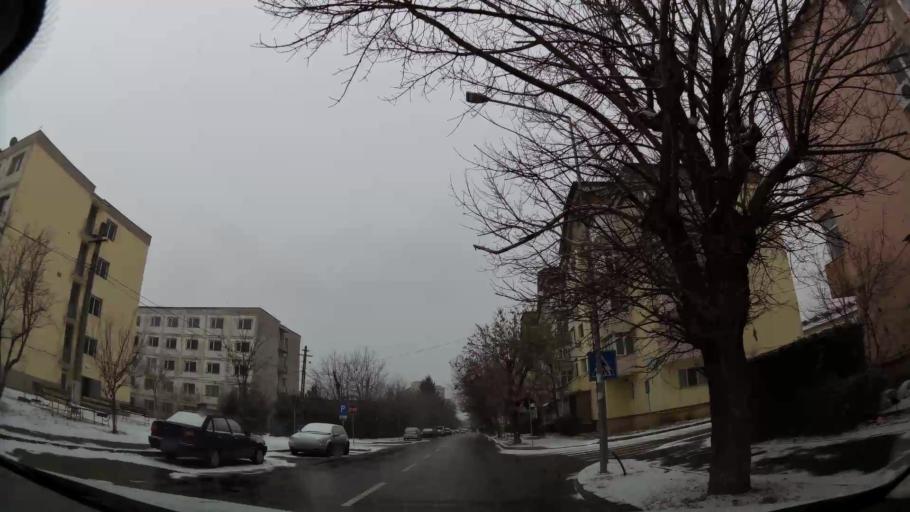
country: RO
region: Dambovita
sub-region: Municipiul Targoviste
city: Targoviste
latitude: 44.9162
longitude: 25.4683
